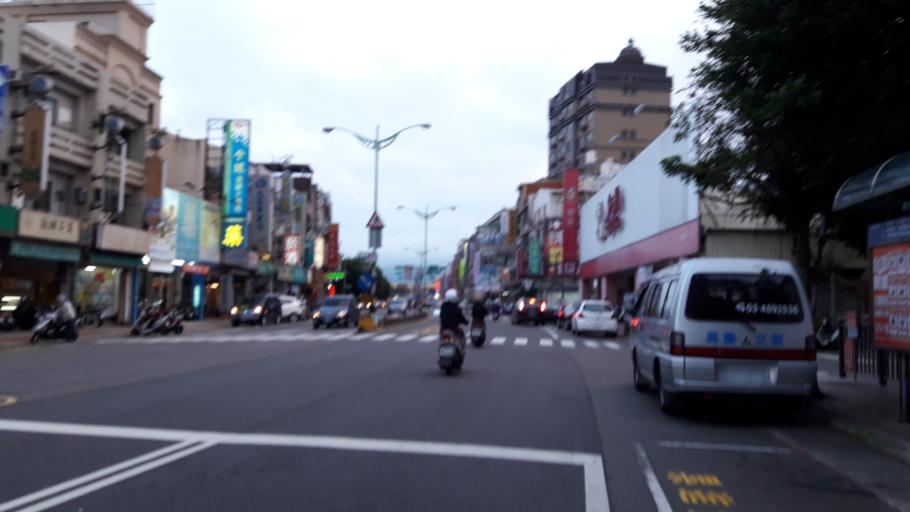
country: TW
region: Taiwan
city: Daxi
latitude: 24.8643
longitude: 121.2170
